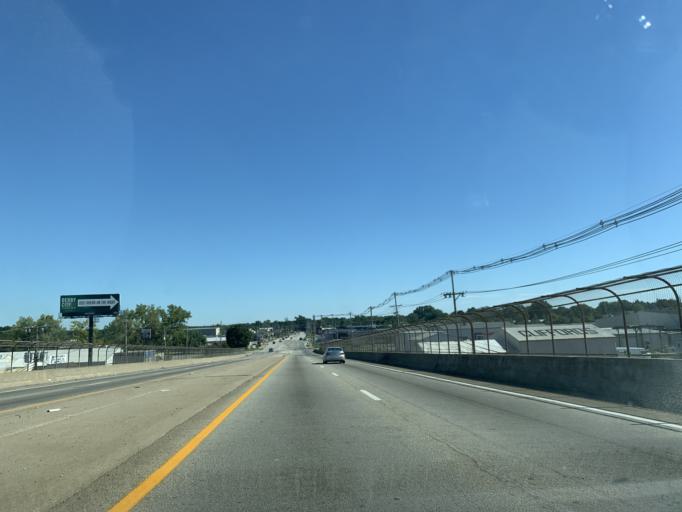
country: US
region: Kentucky
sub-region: Jefferson County
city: Audubon Park
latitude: 38.1903
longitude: -85.7042
